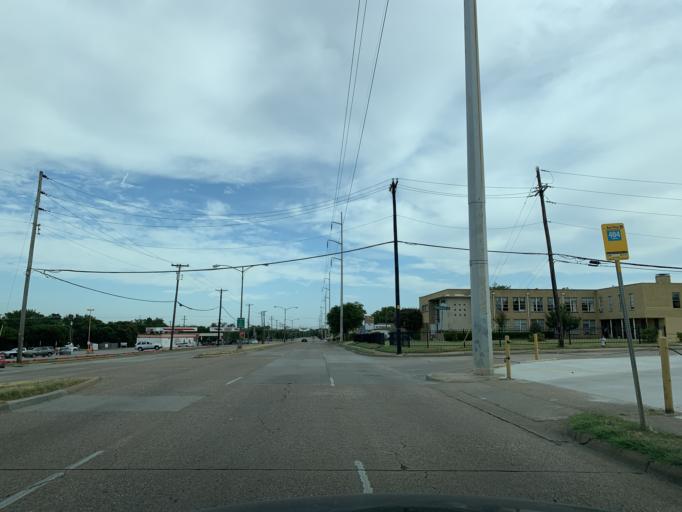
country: US
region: Texas
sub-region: Dallas County
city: Cockrell Hill
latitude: 32.7512
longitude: -96.8740
